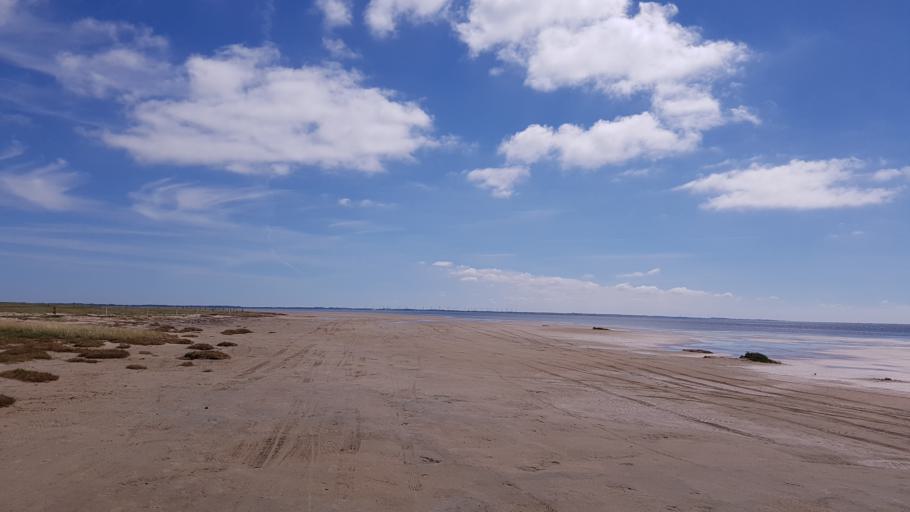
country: DE
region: Schleswig-Holstein
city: List
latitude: 55.0754
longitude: 8.5360
